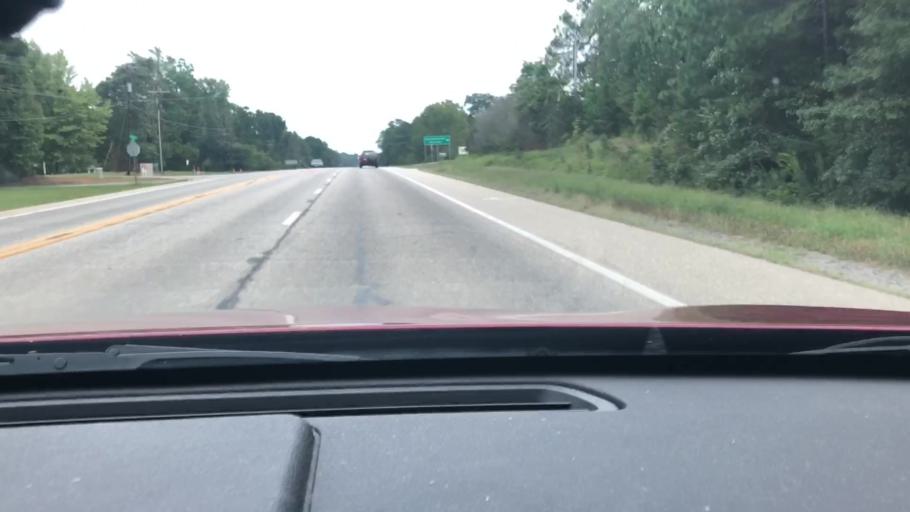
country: US
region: Arkansas
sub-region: Miller County
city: Texarkana
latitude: 33.4296
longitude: -93.9611
